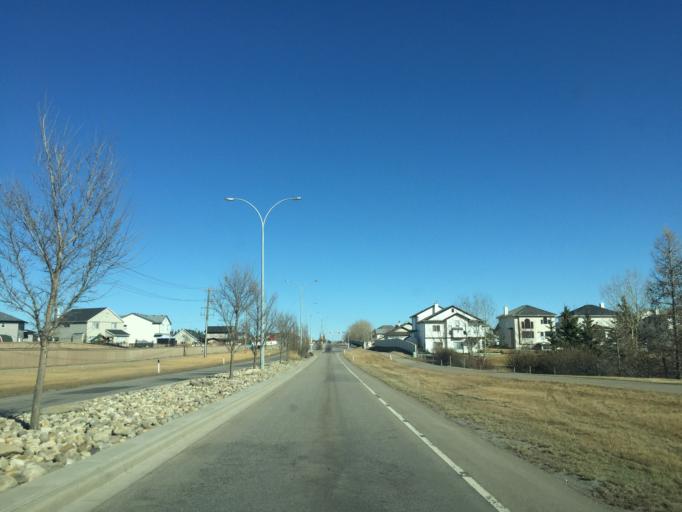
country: CA
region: Alberta
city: Airdrie
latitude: 51.3000
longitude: -114.0445
